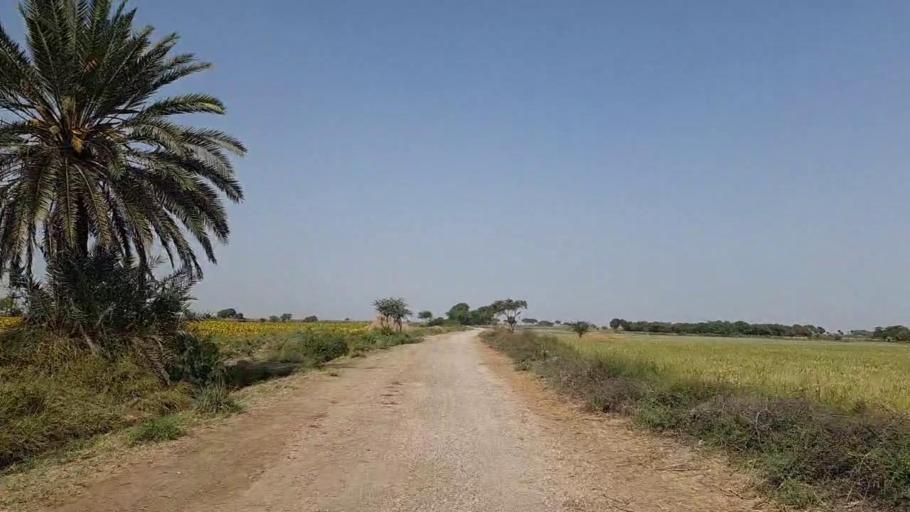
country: PK
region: Sindh
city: Jati
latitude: 24.3448
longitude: 68.3052
